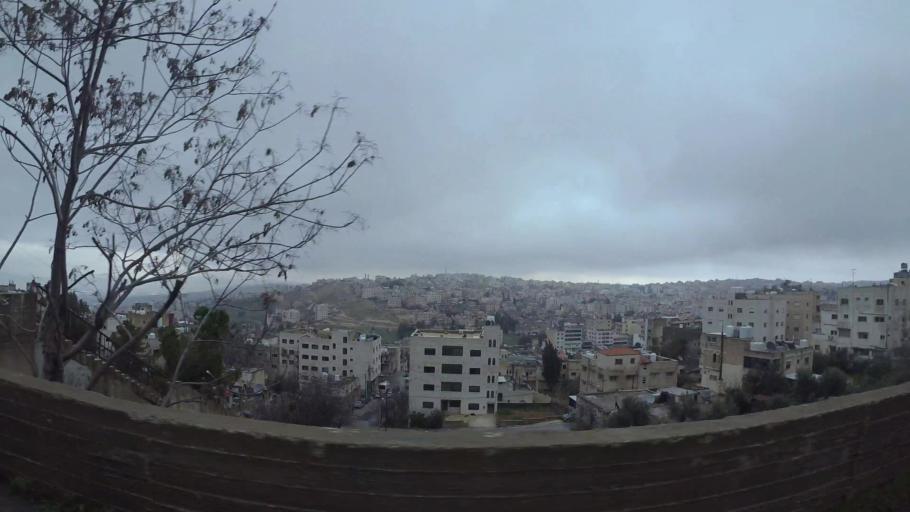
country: JO
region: Amman
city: Al Jubayhah
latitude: 32.0237
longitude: 35.8373
